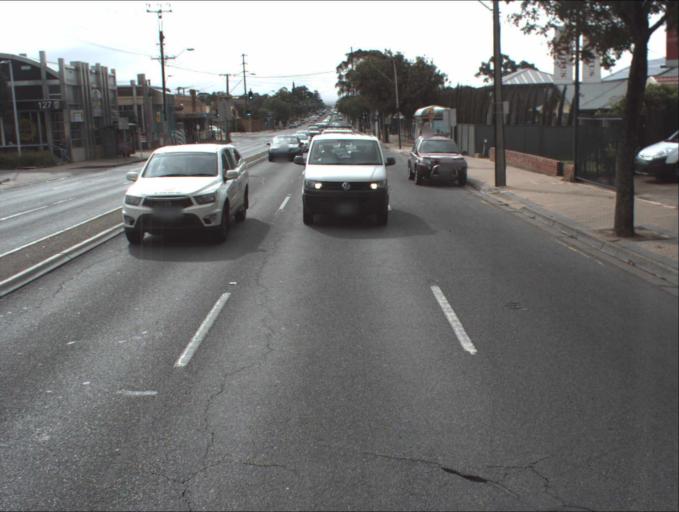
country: AU
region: South Australia
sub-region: Port Adelaide Enfield
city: Klemzig
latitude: -34.8850
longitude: 138.6190
